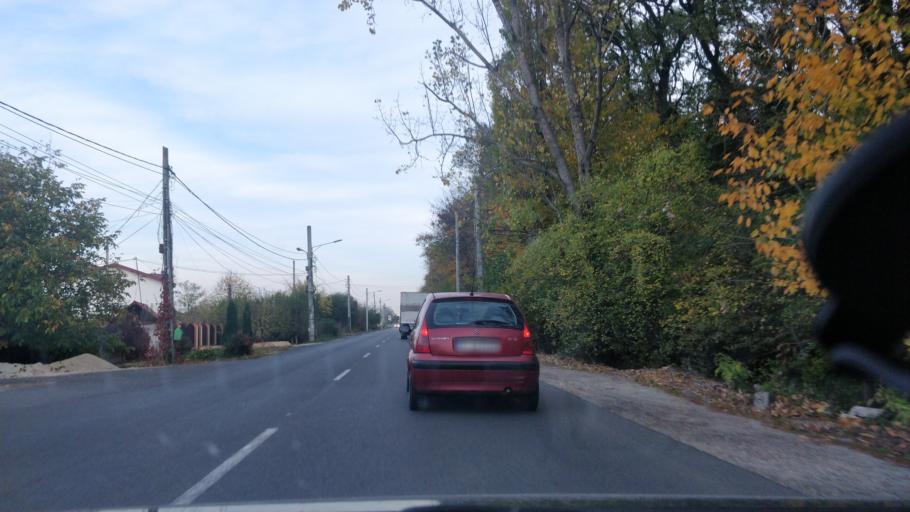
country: RO
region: Ilfov
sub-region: Comuna Ciorogarla
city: Ciorogarla
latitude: 44.4461
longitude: 25.8576
